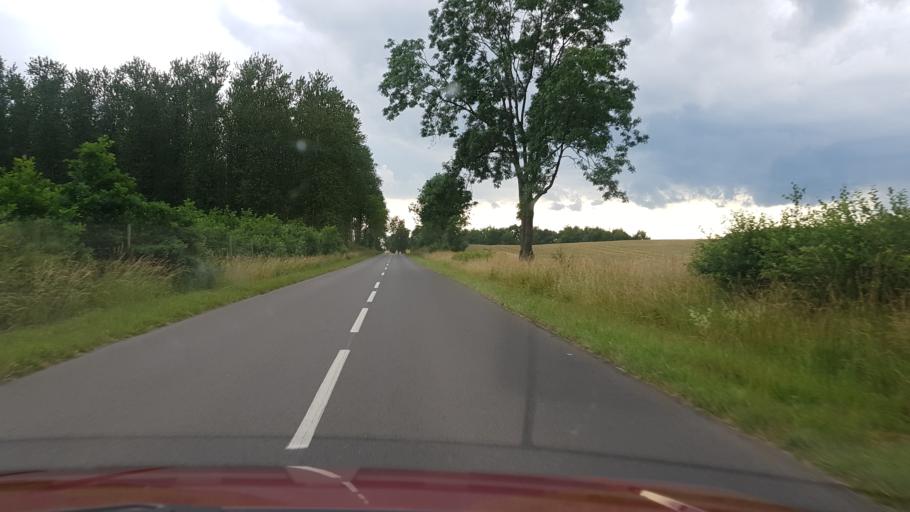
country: PL
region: West Pomeranian Voivodeship
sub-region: Powiat gryficki
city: Gryfice
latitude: 53.8819
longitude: 15.1501
